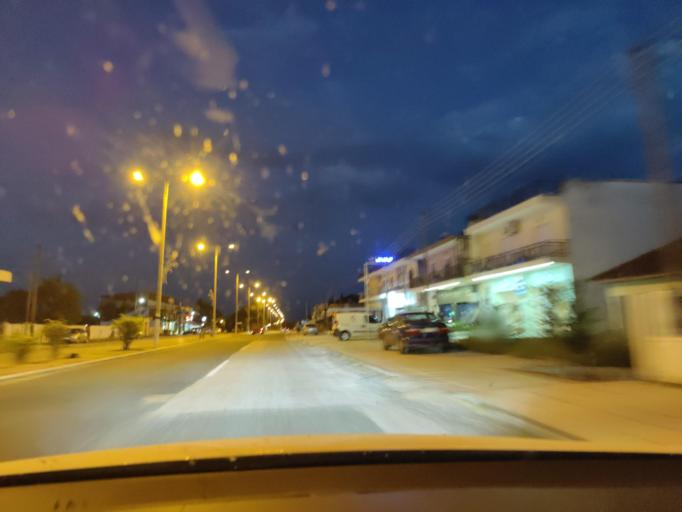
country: GR
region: Central Macedonia
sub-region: Nomos Serron
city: Lefkonas
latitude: 41.0966
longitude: 23.5007
